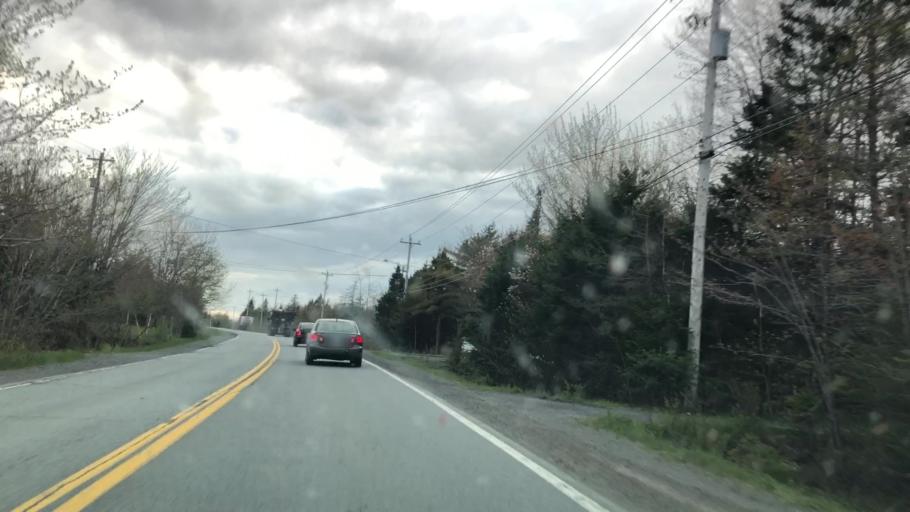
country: CA
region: Nova Scotia
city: Cole Harbour
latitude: 44.7831
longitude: -63.1702
